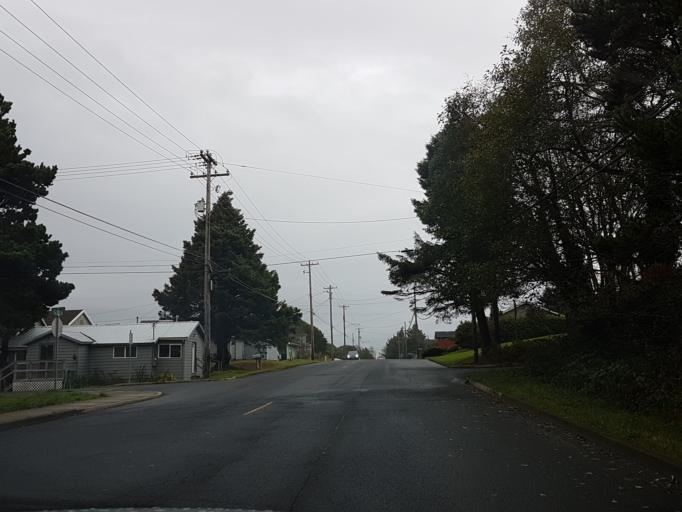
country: US
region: Oregon
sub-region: Lincoln County
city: Newport
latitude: 44.6423
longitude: -124.0557
